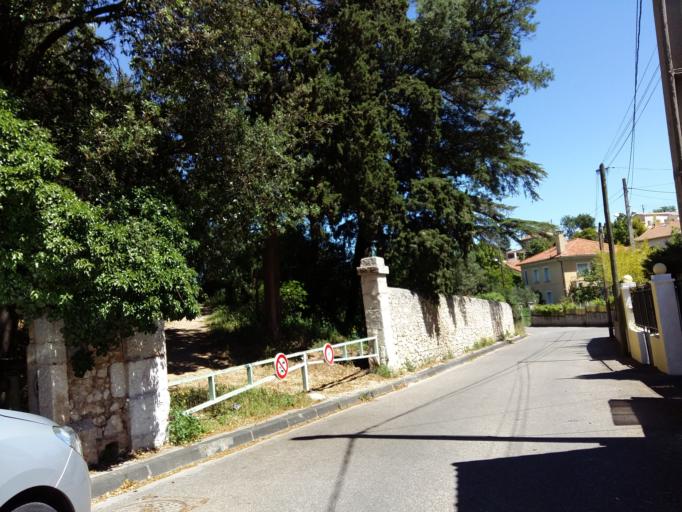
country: FR
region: Provence-Alpes-Cote d'Azur
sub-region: Departement des Bouches-du-Rhone
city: Marseille 11
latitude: 43.2823
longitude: 5.4769
